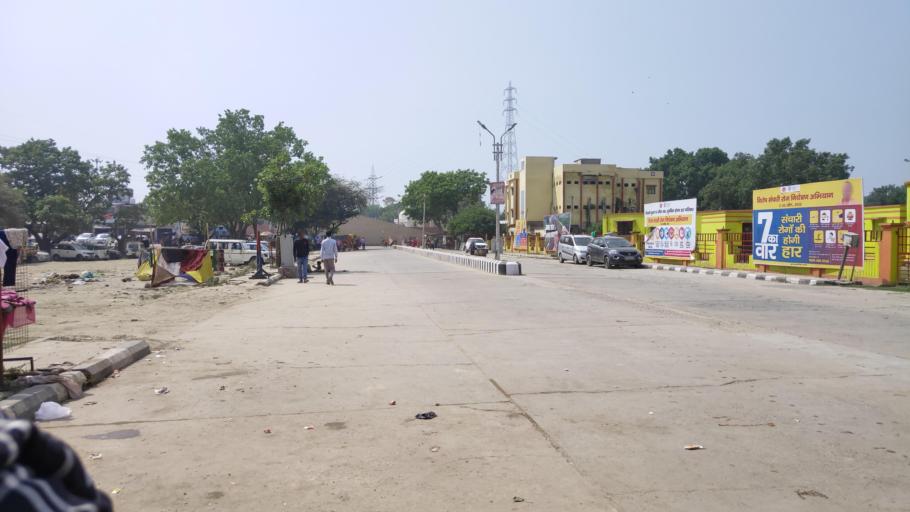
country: IN
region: Uttar Pradesh
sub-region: Faizabad
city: Ayodhya
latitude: 26.8083
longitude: 82.2109
